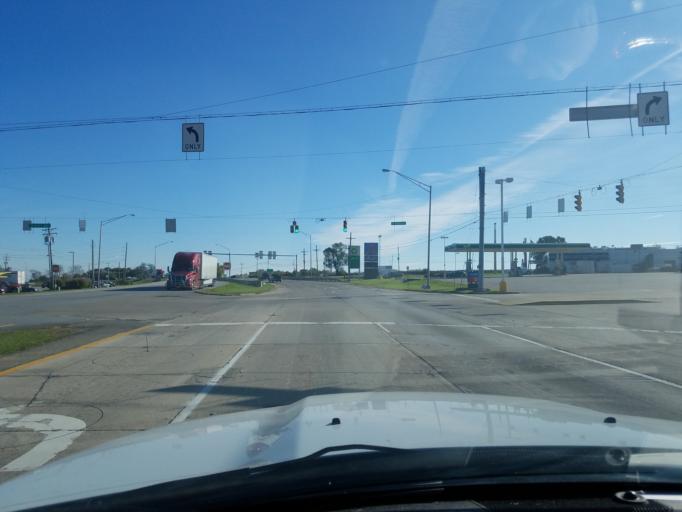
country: US
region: Indiana
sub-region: Jackson County
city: Seymour
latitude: 38.9582
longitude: -85.8380
